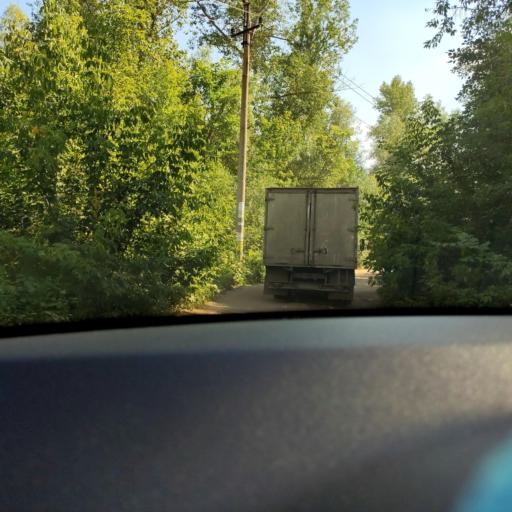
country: RU
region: Samara
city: Volzhskiy
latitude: 53.4358
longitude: 50.1667
